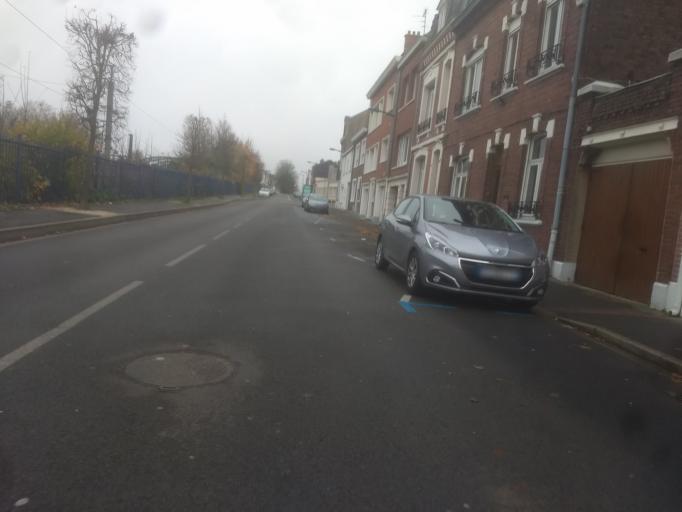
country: FR
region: Nord-Pas-de-Calais
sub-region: Departement du Pas-de-Calais
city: Arras
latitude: 50.2873
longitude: 2.7838
